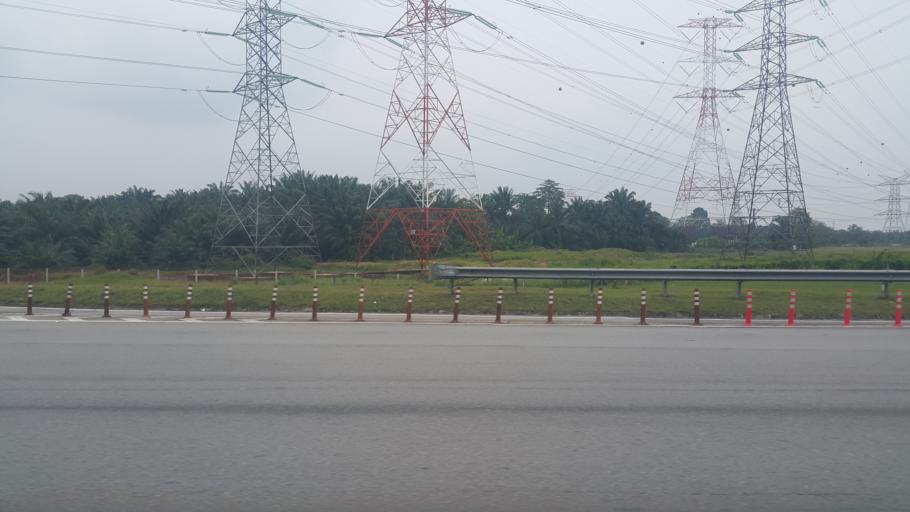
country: MY
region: Putrajaya
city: Putrajaya
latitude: 2.8291
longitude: 101.6609
